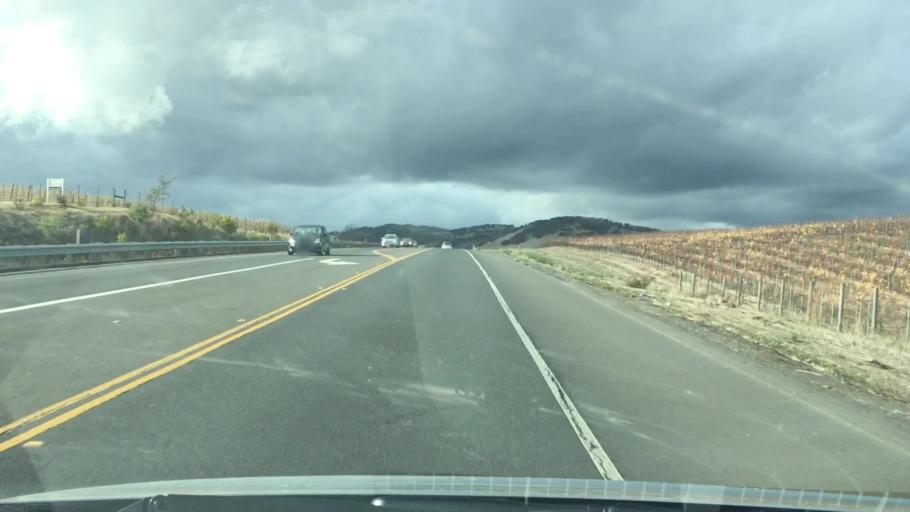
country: US
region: California
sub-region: Napa County
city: Napa
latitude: 38.2572
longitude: -122.3528
